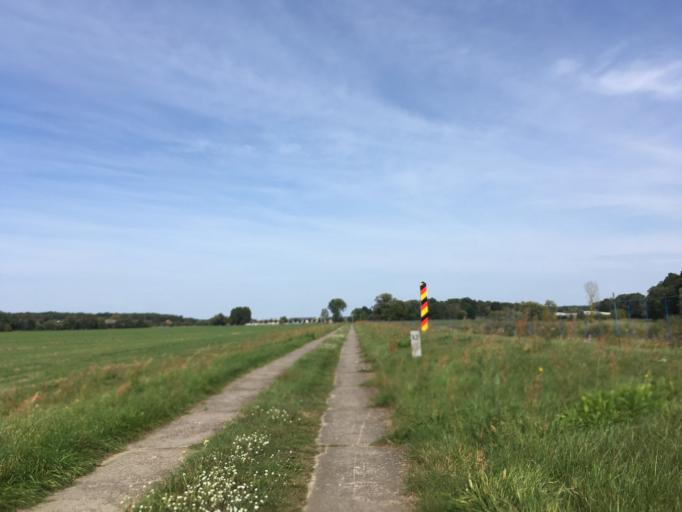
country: PL
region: Lubusz
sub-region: Powiat krosnienski
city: Gubin
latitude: 52.0120
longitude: 14.7251
